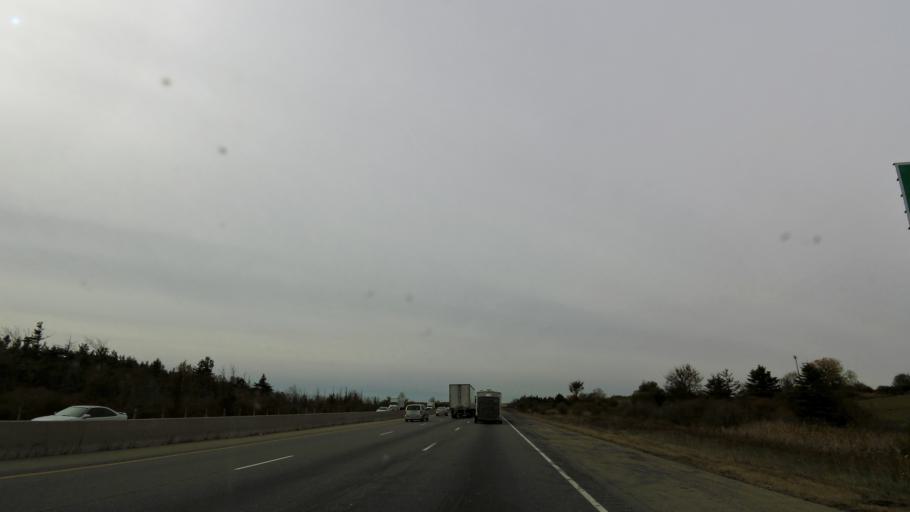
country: CA
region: Ontario
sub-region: Wellington County
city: Guelph
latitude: 43.4434
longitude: -80.2008
